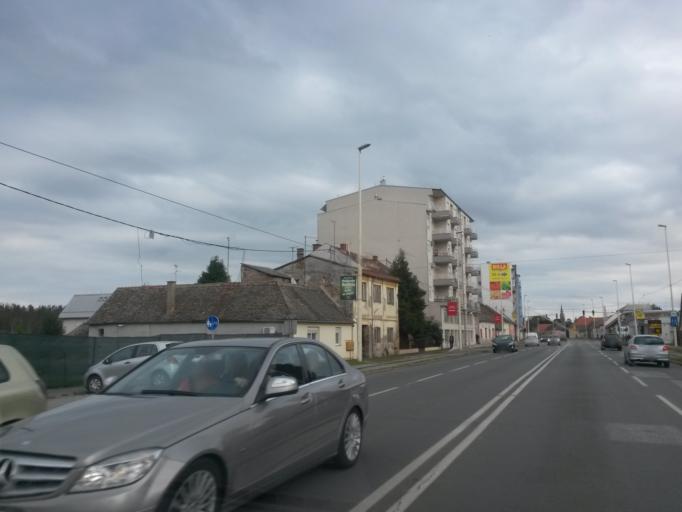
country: HR
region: Osjecko-Baranjska
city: Visnjevac
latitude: 45.5642
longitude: 18.6548
